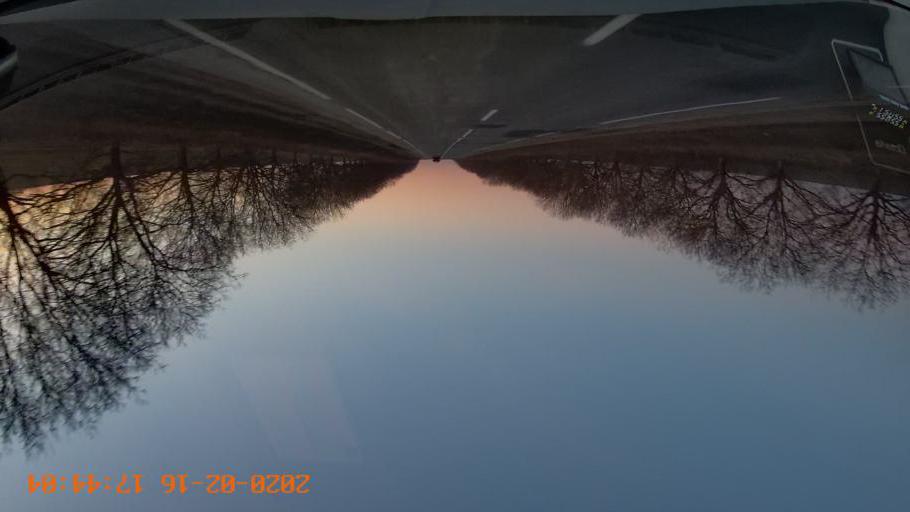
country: MD
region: Riscani
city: Riscani
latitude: 48.0033
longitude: 27.5698
